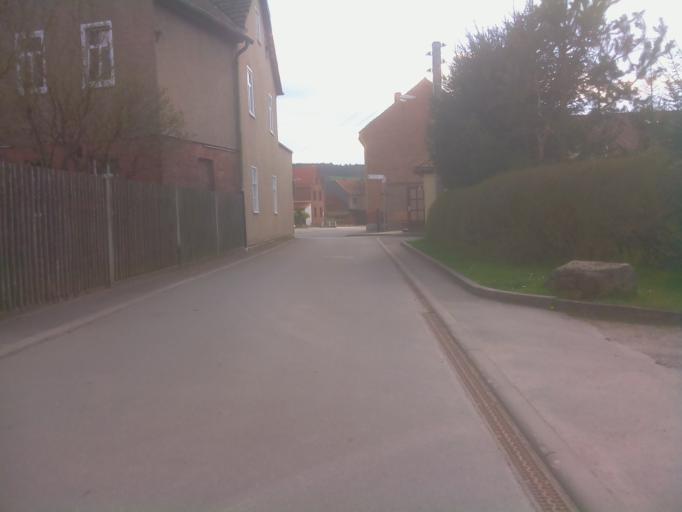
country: DE
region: Thuringia
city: Kleineutersdorf
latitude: 50.7889
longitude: 11.5778
